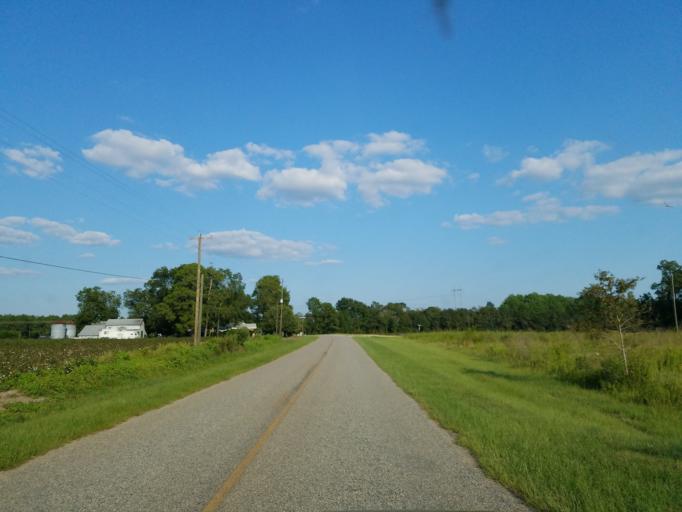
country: US
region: Georgia
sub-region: Cook County
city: Sparks
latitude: 31.2362
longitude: -83.4725
